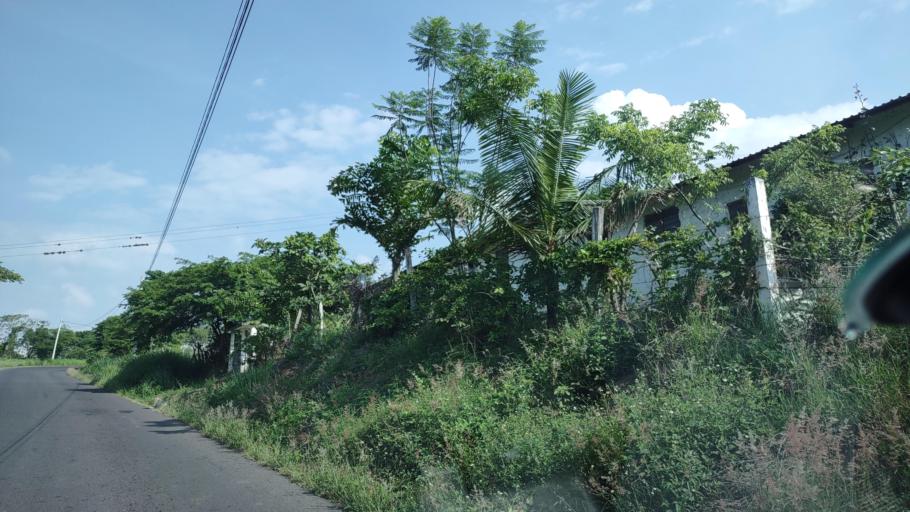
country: MX
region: Veracruz
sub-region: Coatepec
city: Bella Esperanza
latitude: 19.4559
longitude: -96.8346
